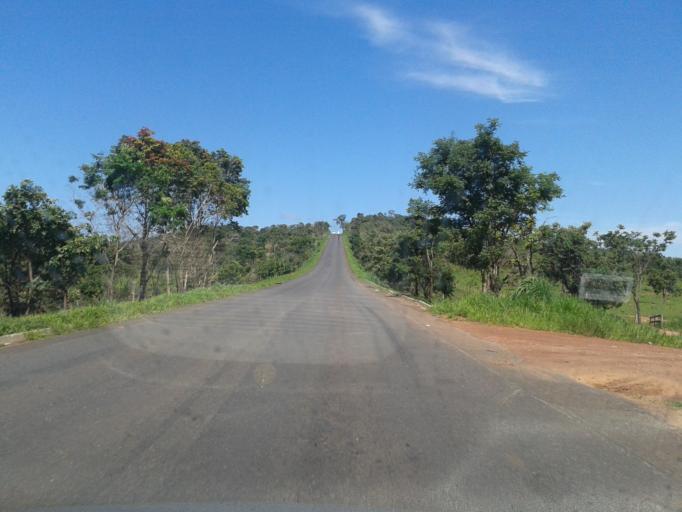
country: BR
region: Goias
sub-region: Bela Vista De Goias
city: Bela Vista de Goias
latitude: -17.1544
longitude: -48.7972
